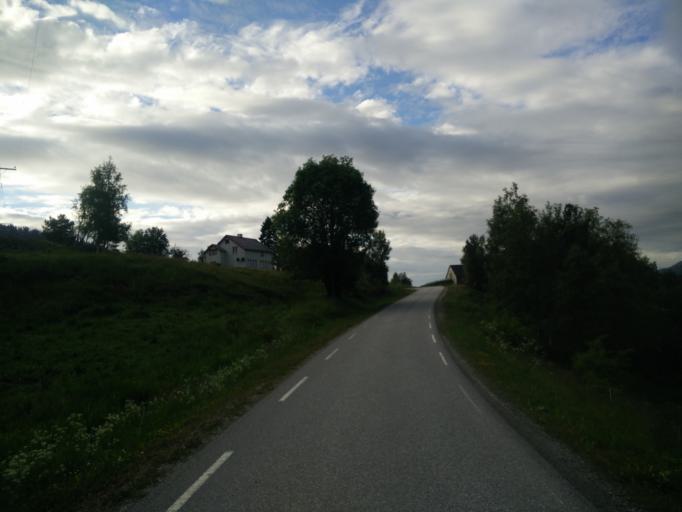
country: NO
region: More og Romsdal
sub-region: Kristiansund
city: Rensvik
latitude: 63.0176
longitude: 7.9630
